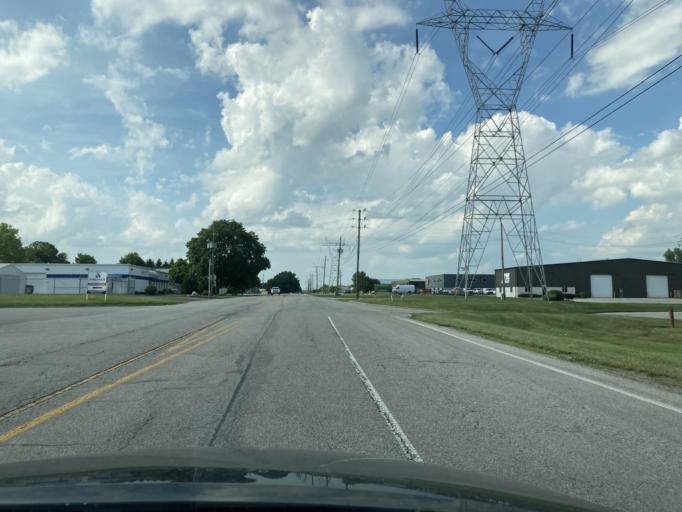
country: US
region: Indiana
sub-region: Marion County
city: Meridian Hills
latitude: 39.8730
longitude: -86.2316
